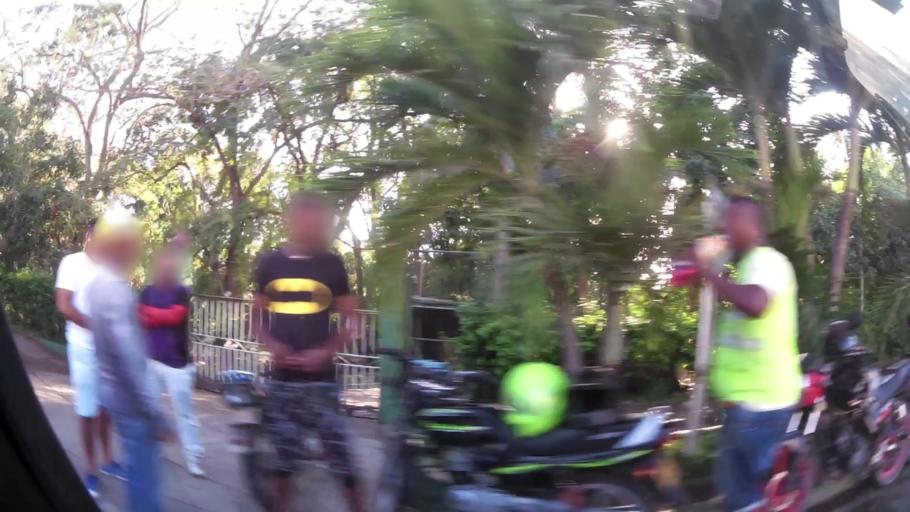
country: CO
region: Bolivar
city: Cartagena
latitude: 10.4020
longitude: -75.4823
